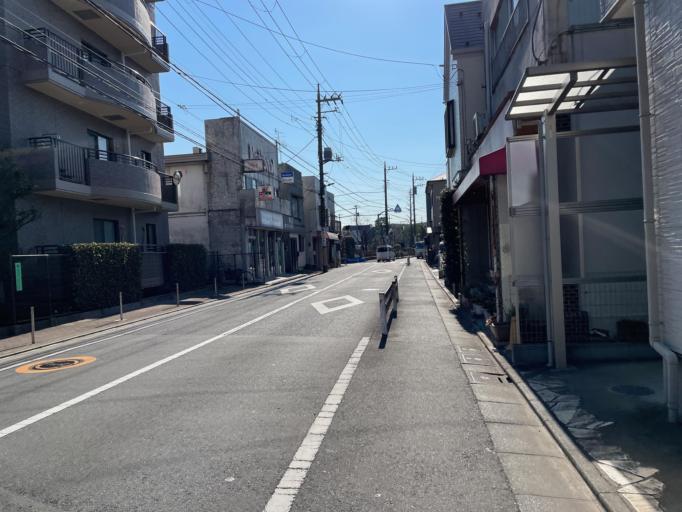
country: JP
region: Saitama
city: Soka
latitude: 35.7970
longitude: 139.7817
